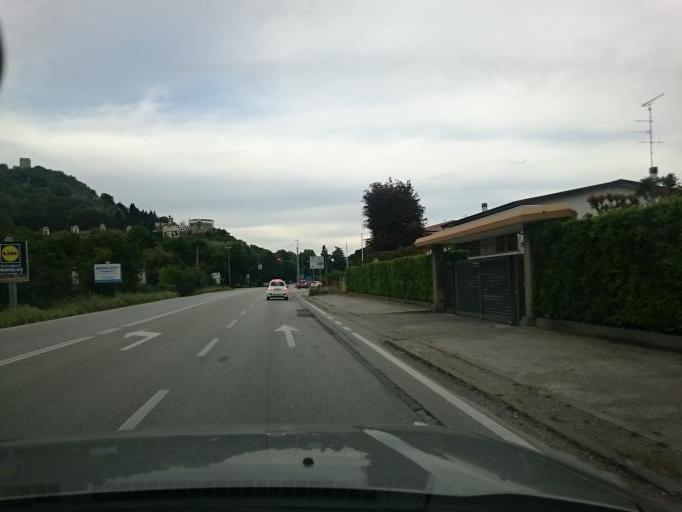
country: IT
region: Veneto
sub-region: Provincia di Padova
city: Monselice
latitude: 45.2363
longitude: 11.7592
